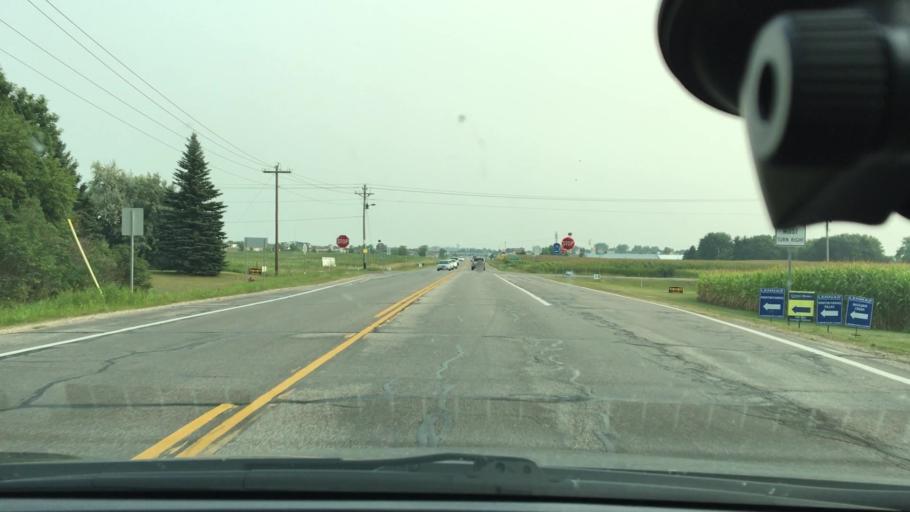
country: US
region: Minnesota
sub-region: Wright County
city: Albertville
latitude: 45.2534
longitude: -93.6633
